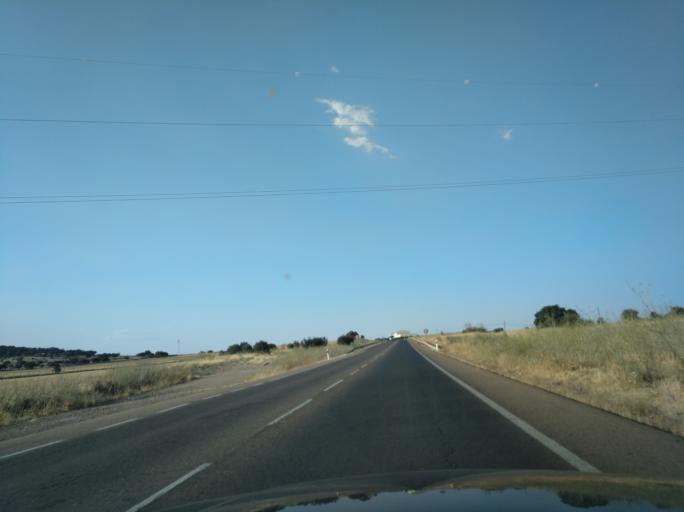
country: ES
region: Extremadura
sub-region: Provincia de Badajoz
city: Olivenza
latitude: 38.7020
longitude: -7.0881
